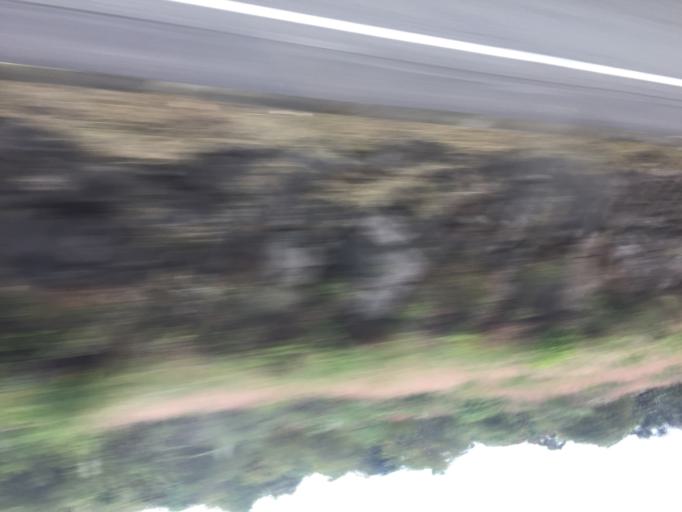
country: MX
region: Jalisco
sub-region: Zapotlan del Rey
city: Zapotlan del Rey
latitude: 20.4995
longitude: -102.9499
